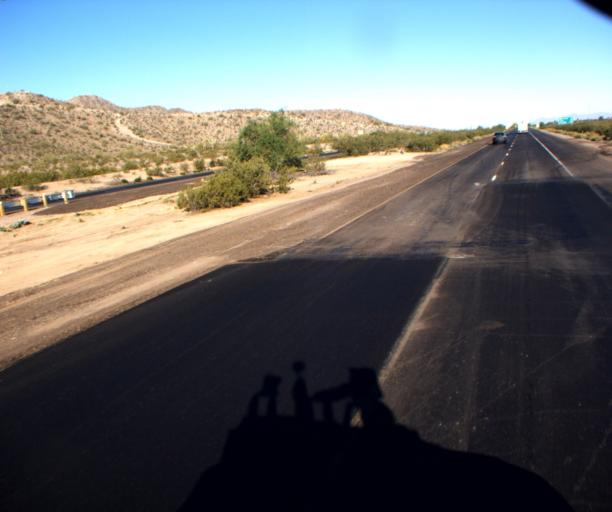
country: US
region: Arizona
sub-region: Pinal County
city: Arizona City
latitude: 32.8250
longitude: -111.6962
